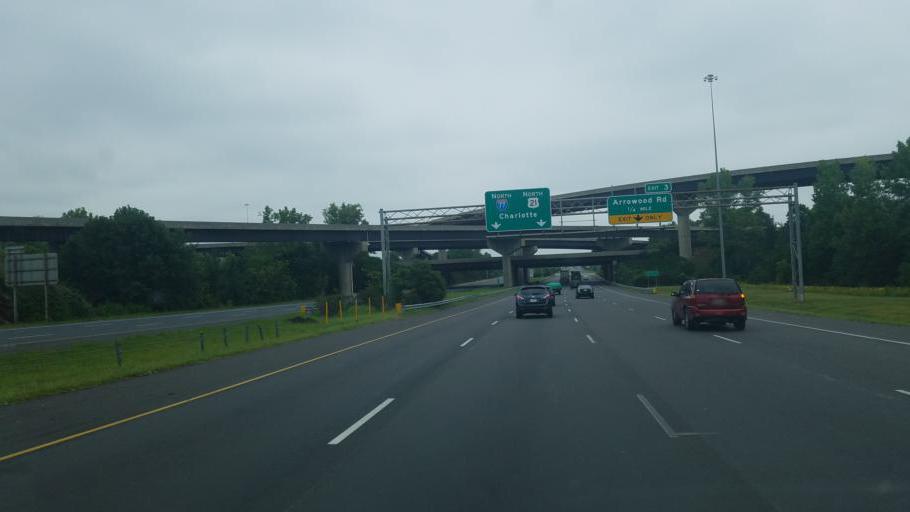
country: US
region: North Carolina
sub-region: Mecklenburg County
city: Pineville
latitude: 35.1235
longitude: -80.9186
